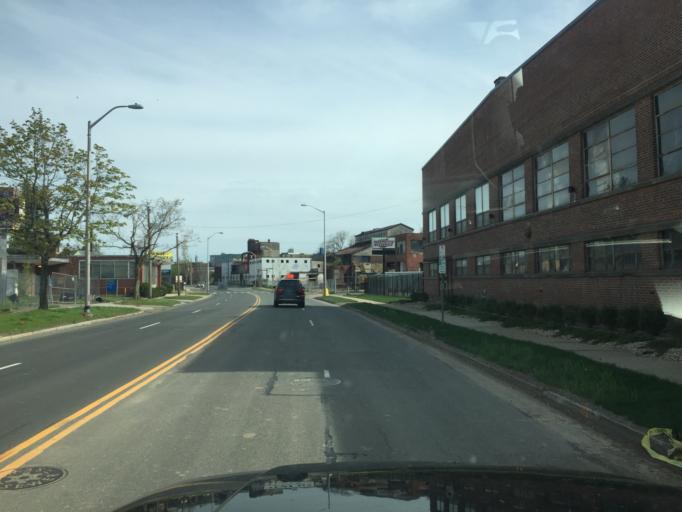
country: US
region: Connecticut
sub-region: Hartford County
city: Hartford
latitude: 41.7829
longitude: -72.7029
